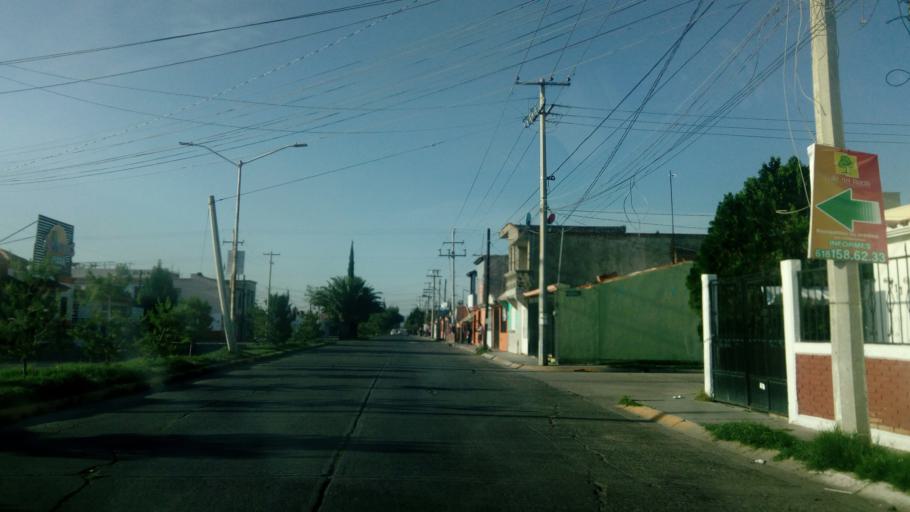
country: MX
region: Durango
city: Victoria de Durango
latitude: 24.0616
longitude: -104.5852
